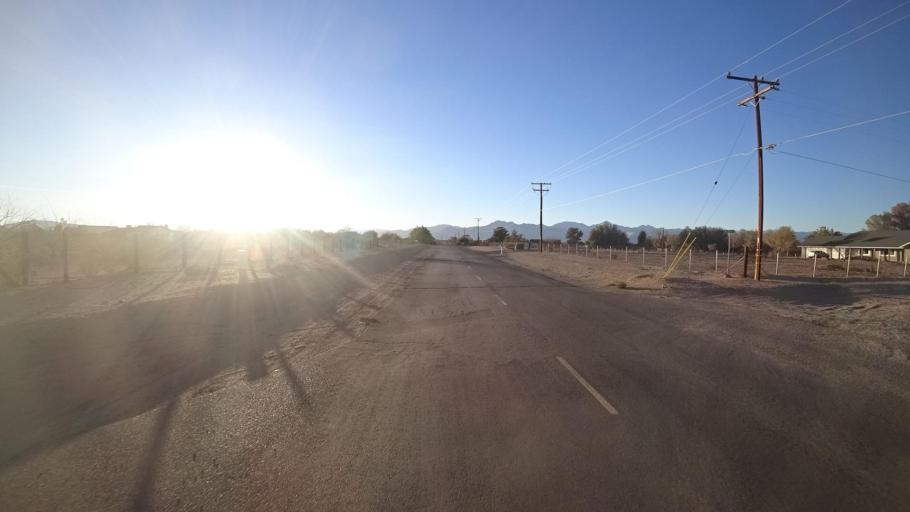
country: US
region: California
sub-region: Kern County
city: Ridgecrest
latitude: 35.6292
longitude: -117.7133
